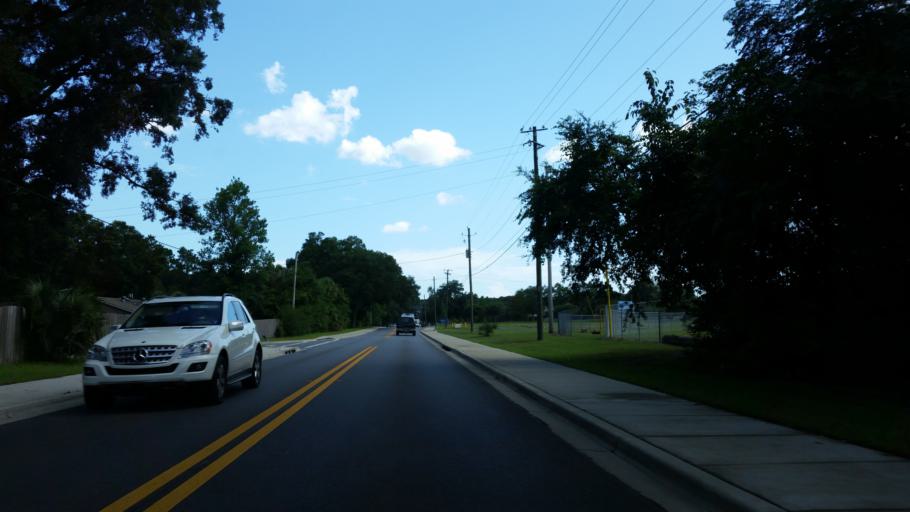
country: US
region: Florida
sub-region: Escambia County
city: Ensley
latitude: 30.5374
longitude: -87.2476
